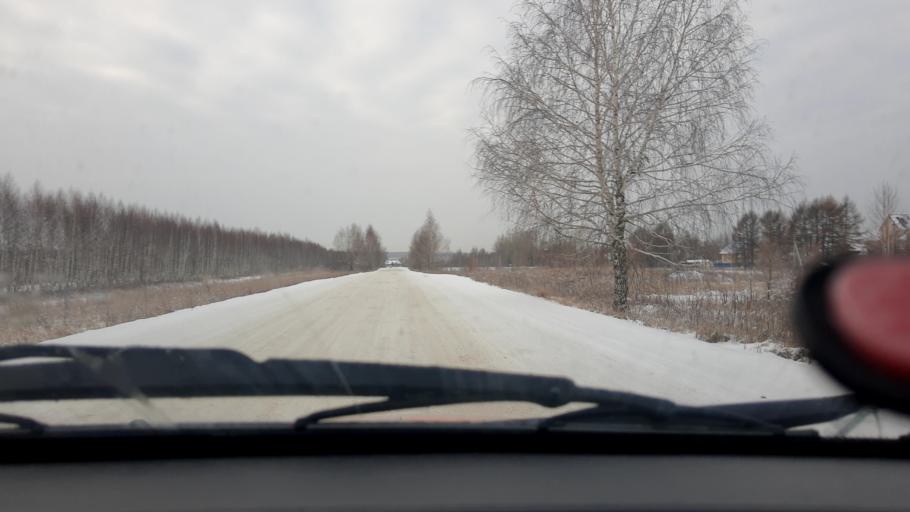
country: RU
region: Bashkortostan
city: Iglino
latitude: 54.7498
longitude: 56.2835
